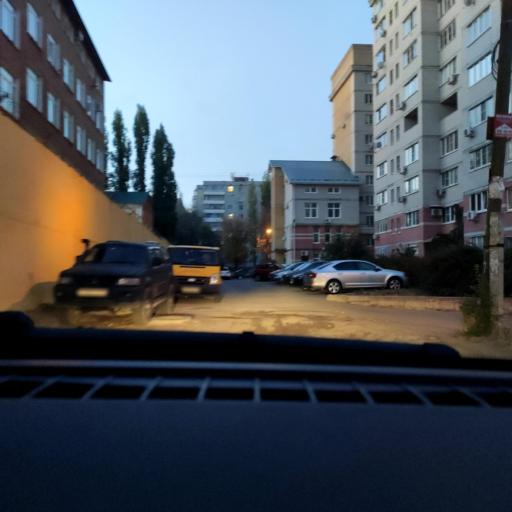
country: RU
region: Voronezj
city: Voronezh
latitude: 51.6758
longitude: 39.2464
